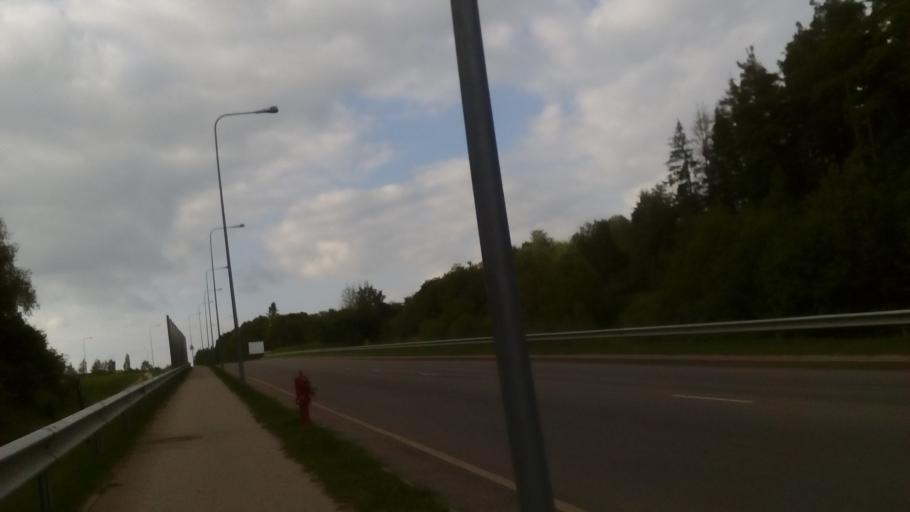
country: LT
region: Alytaus apskritis
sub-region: Alytus
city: Alytus
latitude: 54.4228
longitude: 24.0359
